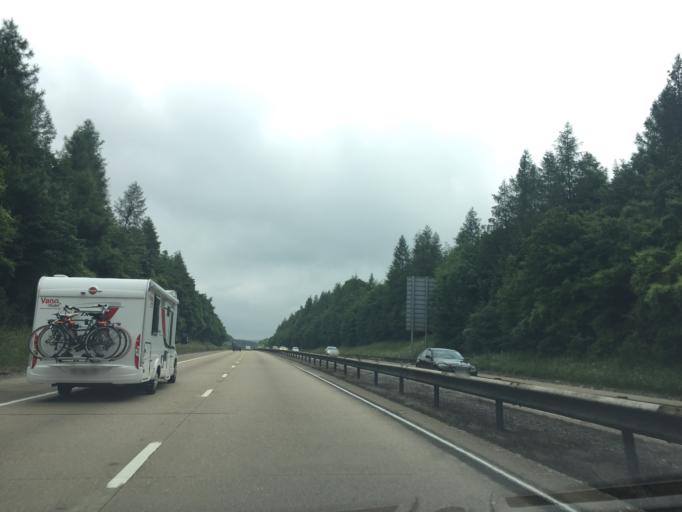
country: GB
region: England
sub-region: Hampshire
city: Kings Worthy
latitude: 51.1279
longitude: -1.2494
